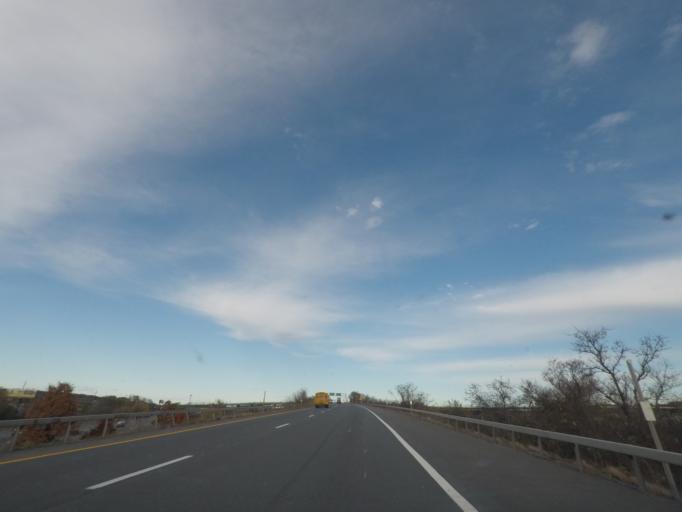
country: US
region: New York
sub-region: Rensselaer County
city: Rensselaer
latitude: 42.6631
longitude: -73.7355
